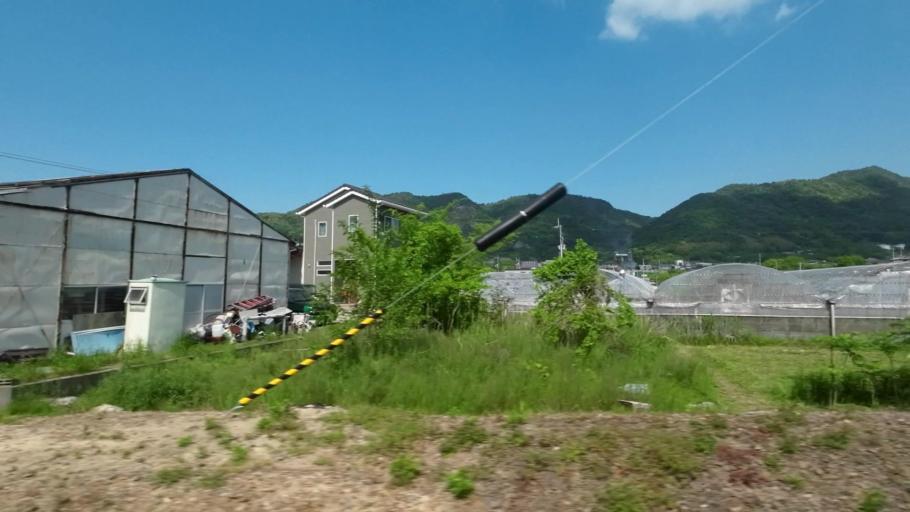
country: JP
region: Kagawa
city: Kan'onjicho
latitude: 34.1453
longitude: 133.6861
